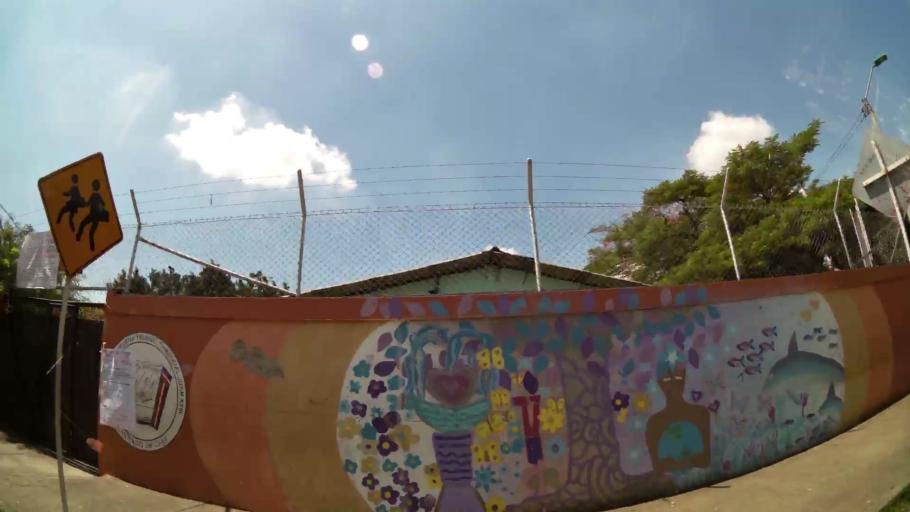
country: CO
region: Valle del Cauca
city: Cali
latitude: 3.4301
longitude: -76.5014
